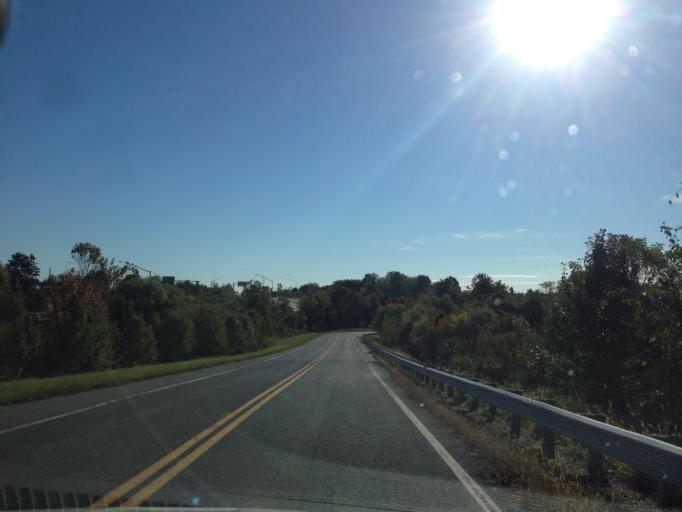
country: US
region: Maryland
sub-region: Howard County
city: Fulton
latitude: 39.1461
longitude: -76.9072
